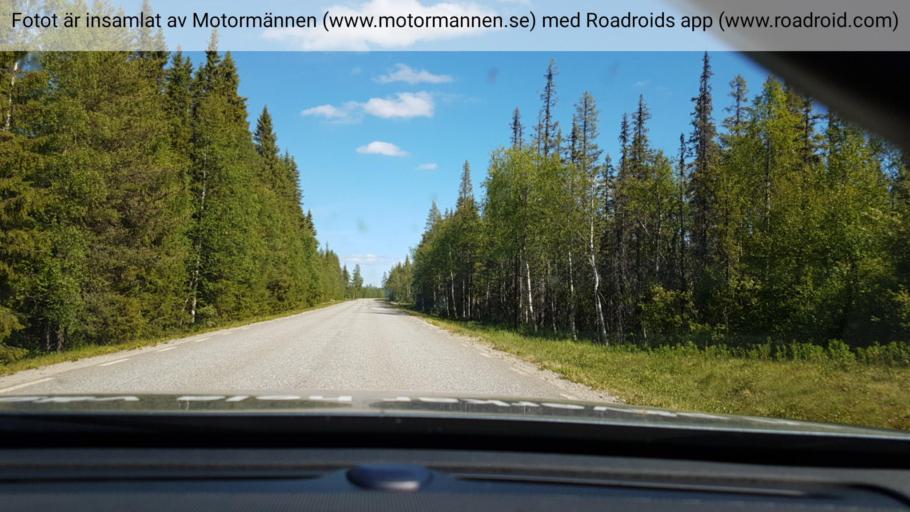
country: SE
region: Vaesterbotten
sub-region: Lycksele Kommun
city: Soderfors
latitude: 64.6334
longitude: 17.9666
